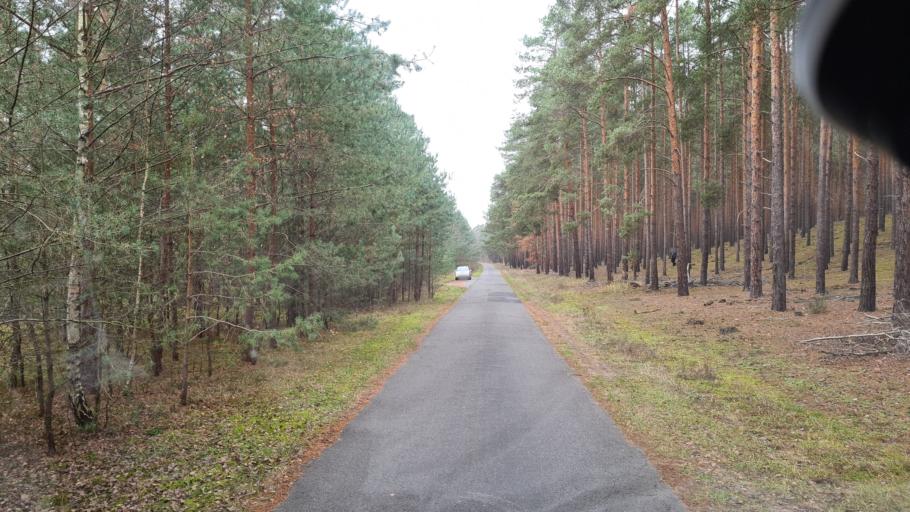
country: DE
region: Brandenburg
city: Schenkendobern
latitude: 51.9743
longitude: 14.6415
